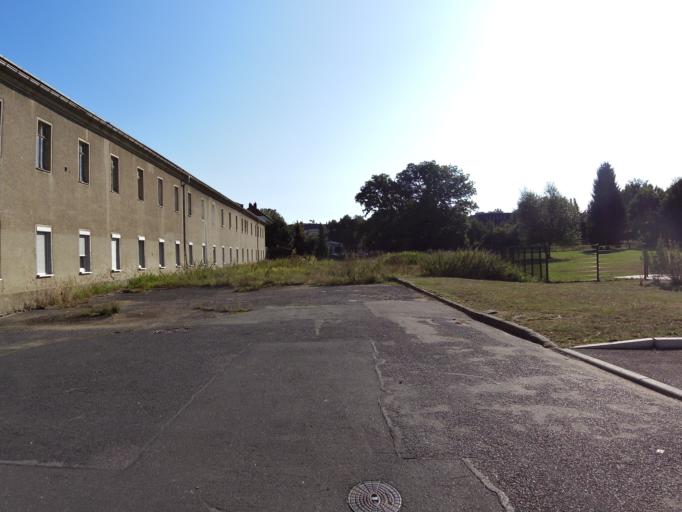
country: DE
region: Saxony
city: Dobeln
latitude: 51.1196
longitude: 13.1267
